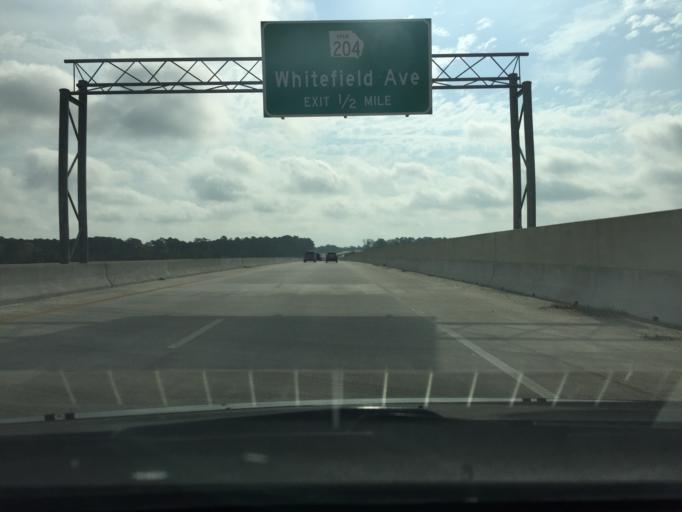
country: US
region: Georgia
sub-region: Chatham County
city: Montgomery
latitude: 31.9752
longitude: -81.1195
